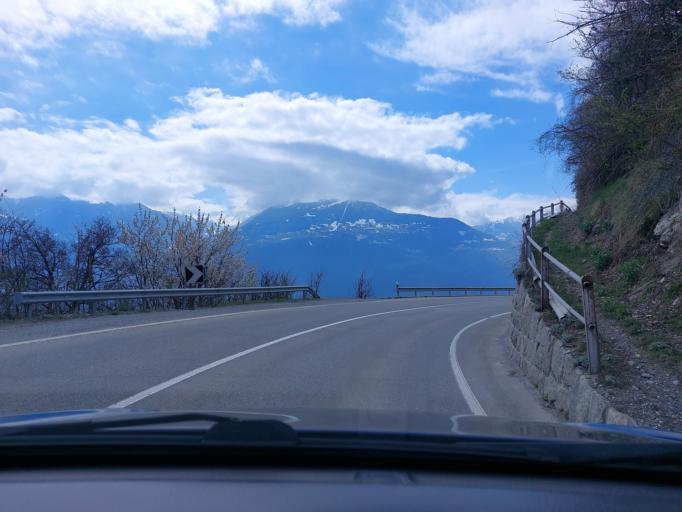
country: CH
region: Valais
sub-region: Conthey District
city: Conthey
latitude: 46.2469
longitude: 7.3031
